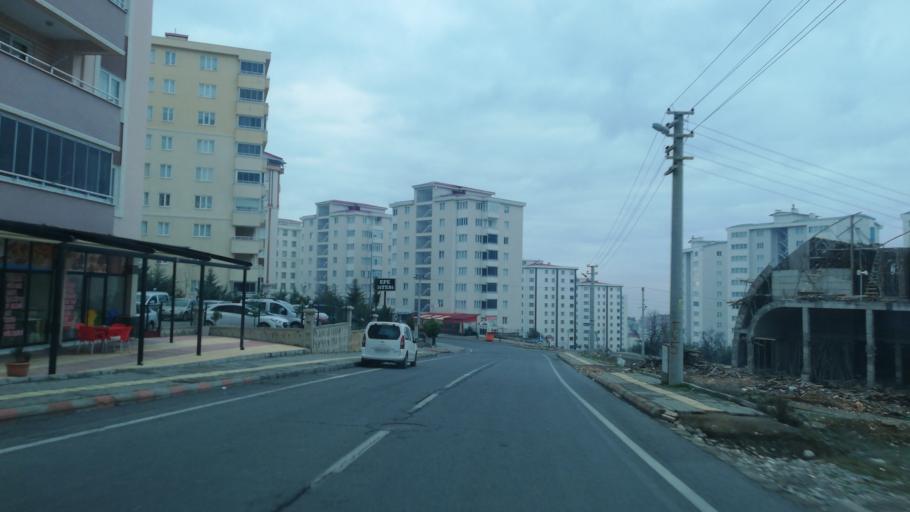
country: TR
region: Kahramanmaras
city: Kahramanmaras
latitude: 37.5987
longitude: 36.8881
